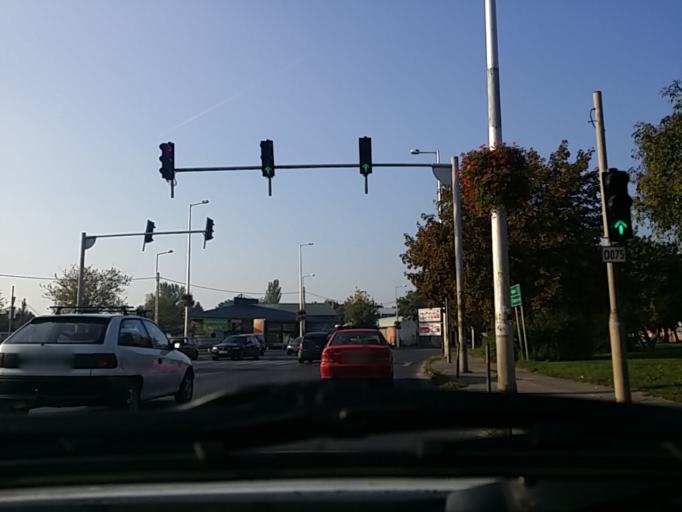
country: HU
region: Pest
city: Szentendre
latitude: 47.6601
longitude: 19.0764
